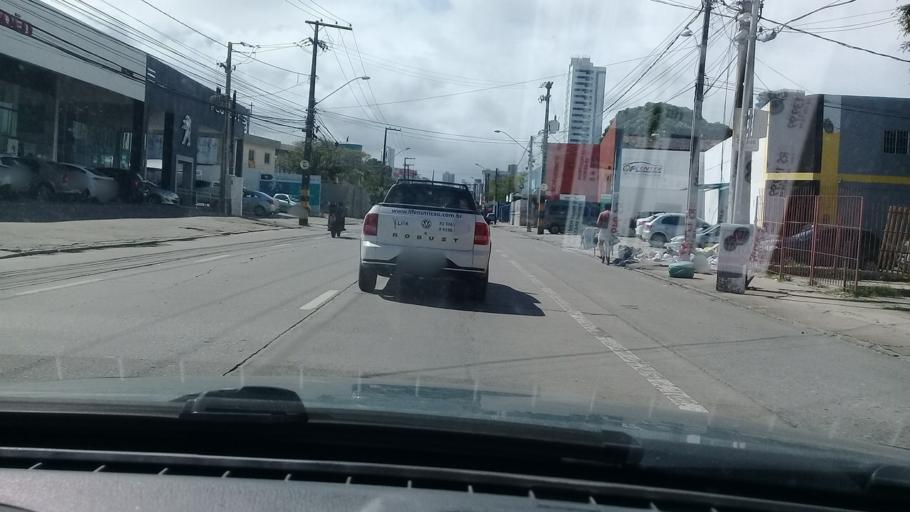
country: BR
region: Pernambuco
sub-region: Recife
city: Recife
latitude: -8.0672
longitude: -34.9084
